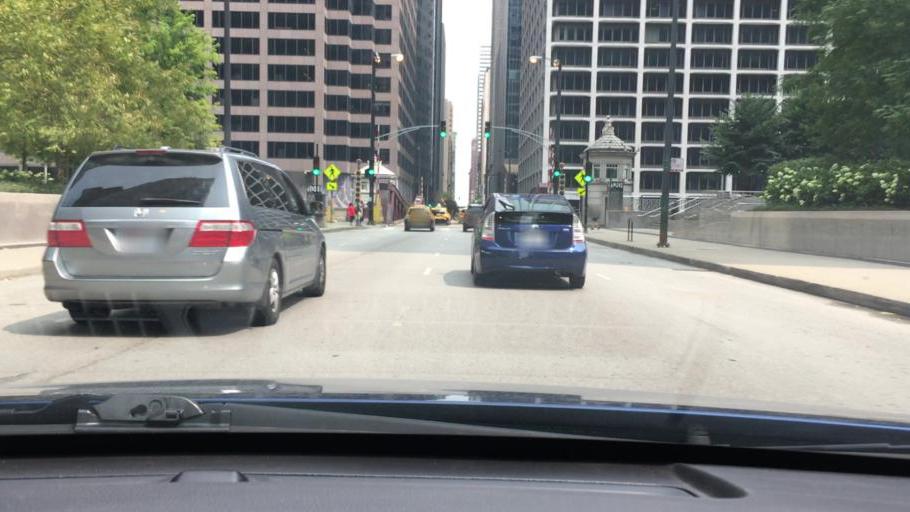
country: US
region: Illinois
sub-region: Cook County
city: Chicago
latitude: 41.8806
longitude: -87.6396
